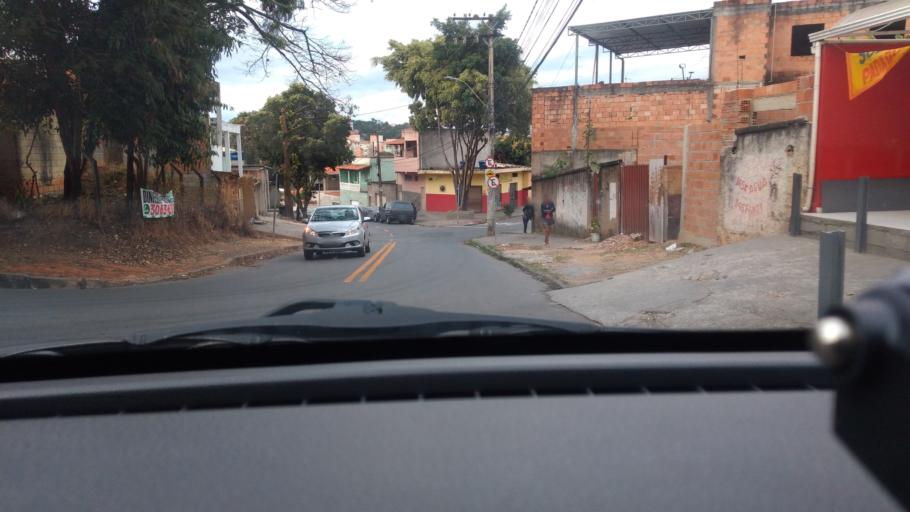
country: BR
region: Minas Gerais
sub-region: Santa Luzia
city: Santa Luzia
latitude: -19.8125
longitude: -43.9384
